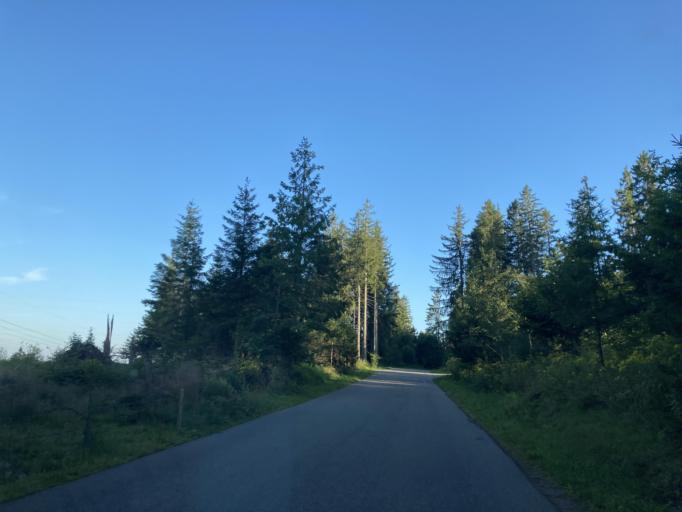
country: DE
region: Baden-Wuerttemberg
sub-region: Freiburg Region
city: Schonach im Schwarzwald
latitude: 48.1659
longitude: 8.1862
